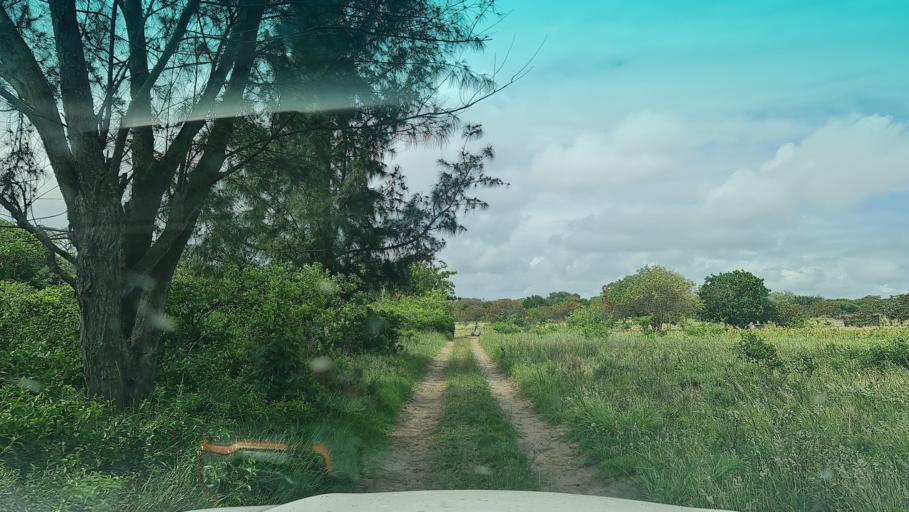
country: MZ
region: Maputo
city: Manhica
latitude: -25.3965
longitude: 33.0282
